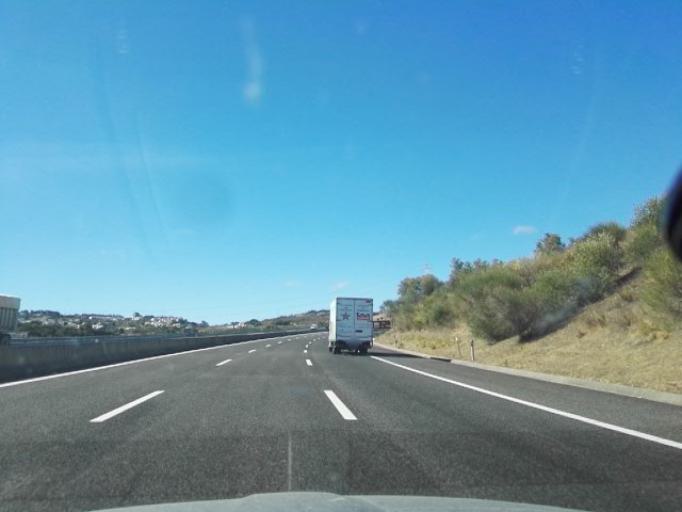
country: PT
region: Lisbon
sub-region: Vila Franca de Xira
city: Castanheira do Ribatejo
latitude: 38.9985
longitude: -9.0165
